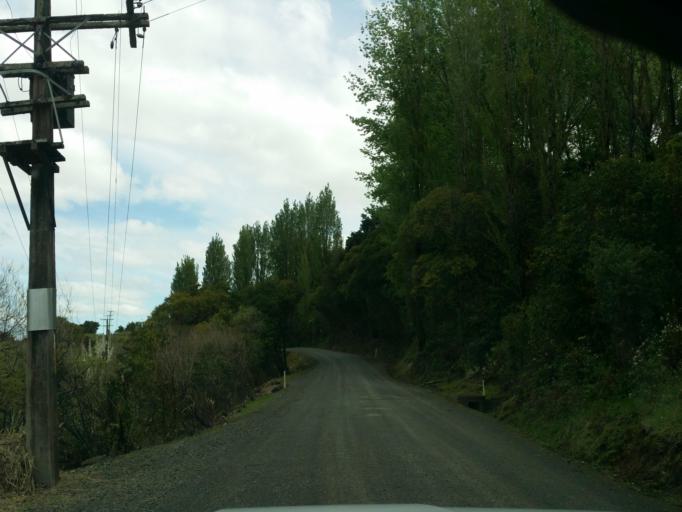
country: NZ
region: Northland
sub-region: Whangarei
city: Maungatapere
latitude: -35.9001
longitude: 174.1121
